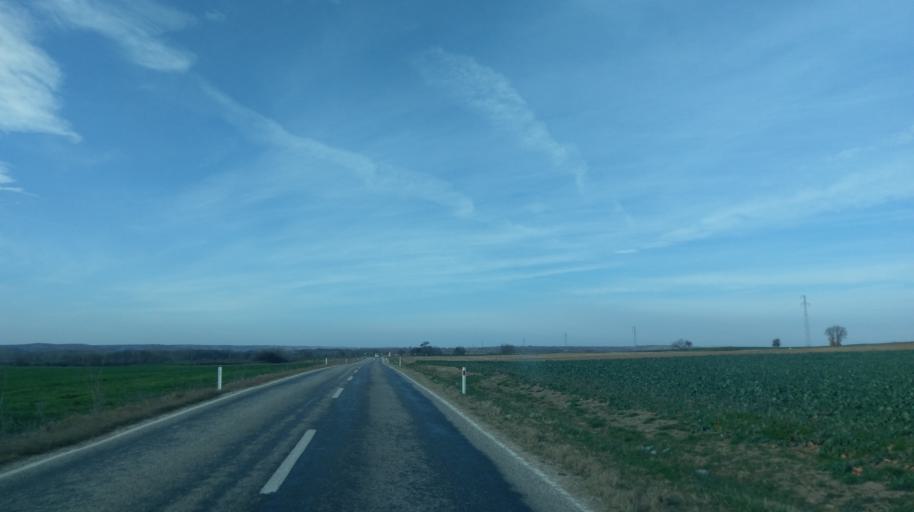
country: TR
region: Kirklareli
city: Pehlivankoy
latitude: 41.3692
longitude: 26.9841
